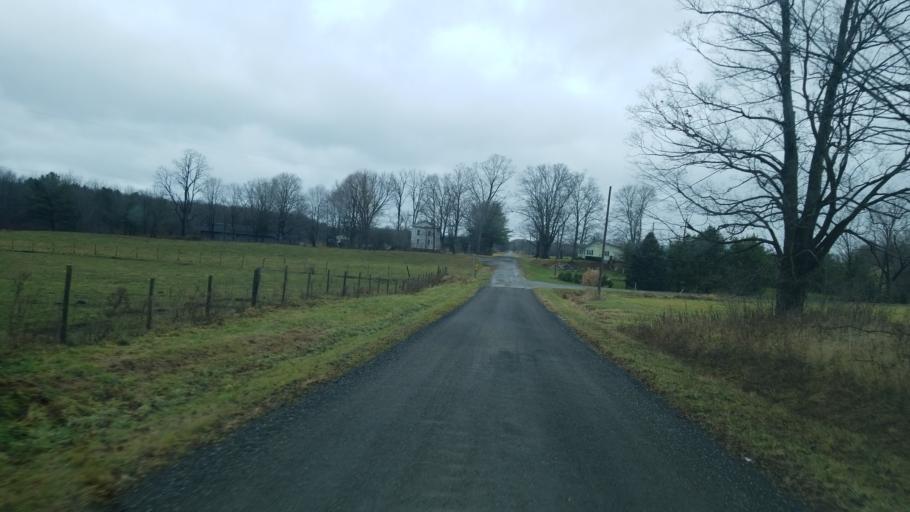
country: US
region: Ohio
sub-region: Ashtabula County
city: Andover
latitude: 41.6223
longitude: -80.6243
